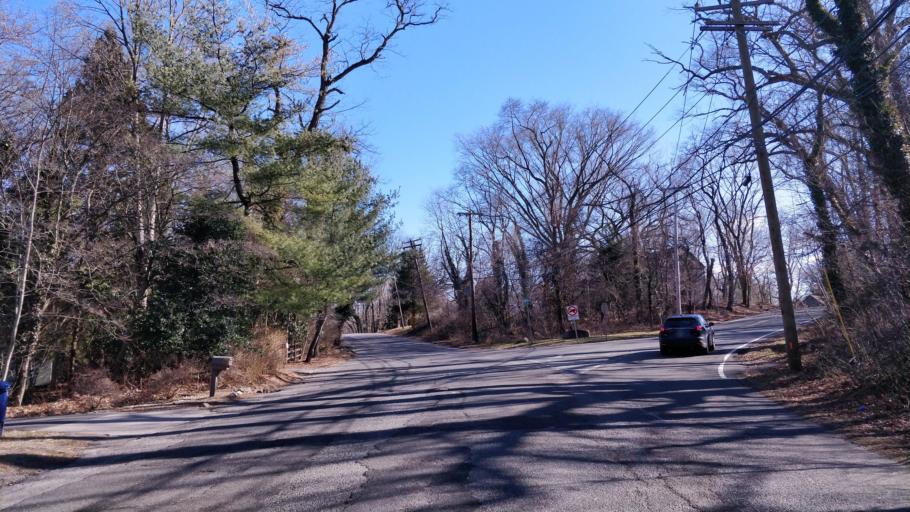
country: US
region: New York
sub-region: Suffolk County
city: Port Jefferson
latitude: 40.9389
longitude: -73.0855
